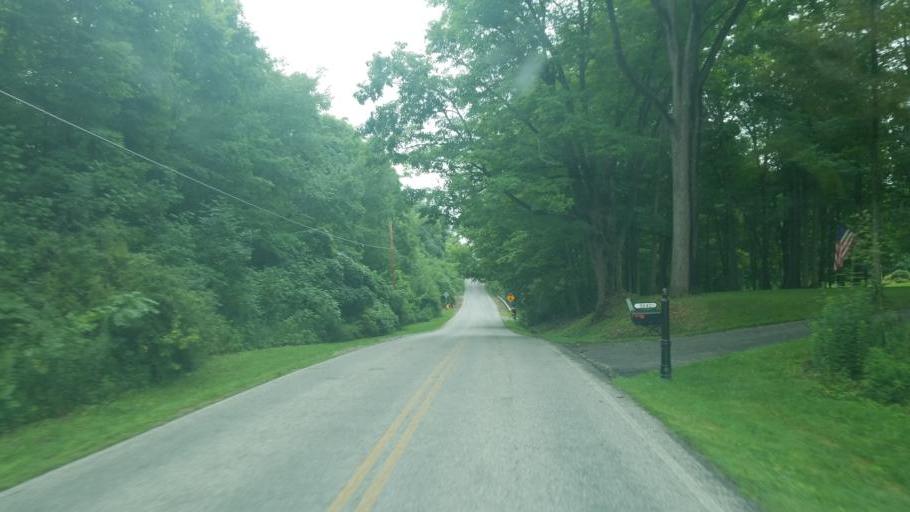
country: US
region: Ohio
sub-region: Delaware County
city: Sunbury
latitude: 40.2948
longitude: -82.8750
